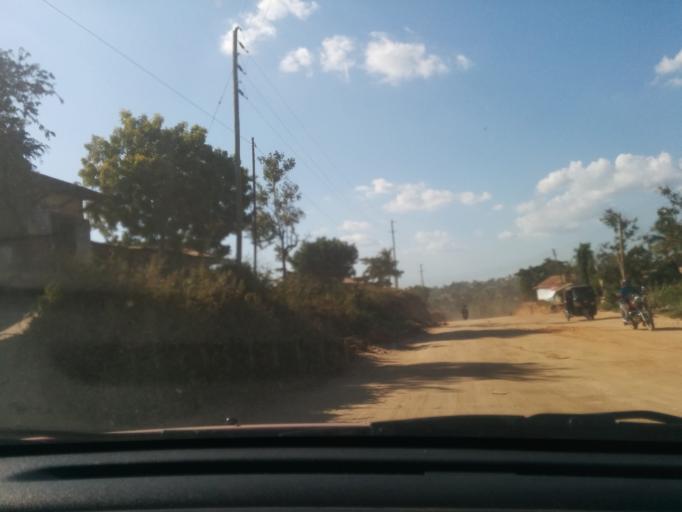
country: TZ
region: Dar es Salaam
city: Magomeni
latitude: -6.7697
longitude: 39.1203
